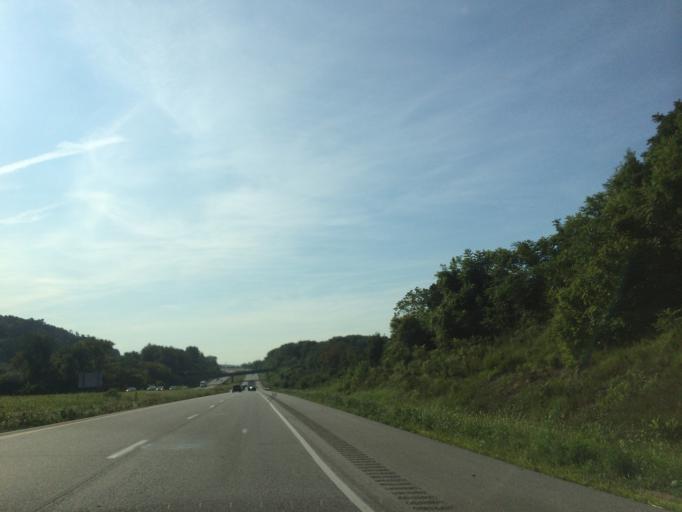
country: US
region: Pennsylvania
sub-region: Lancaster County
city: Columbia
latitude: 40.0440
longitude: -76.4869
